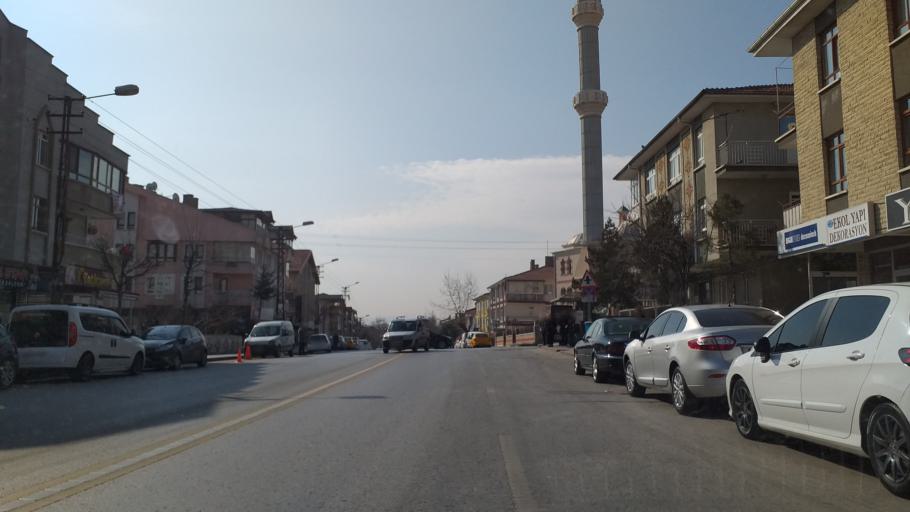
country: TR
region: Ankara
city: Ankara
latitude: 39.9872
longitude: 32.8543
